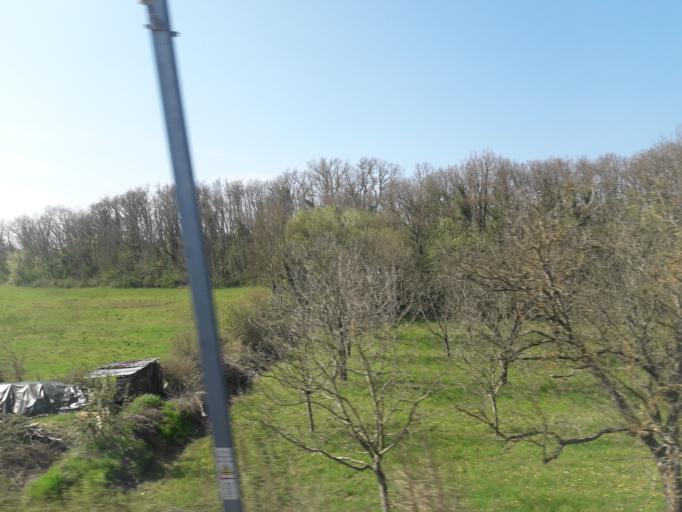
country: FR
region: Rhone-Alpes
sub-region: Departement de l'Isere
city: Saint-Hilaire-du-Rosier
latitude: 45.0771
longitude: 5.2545
